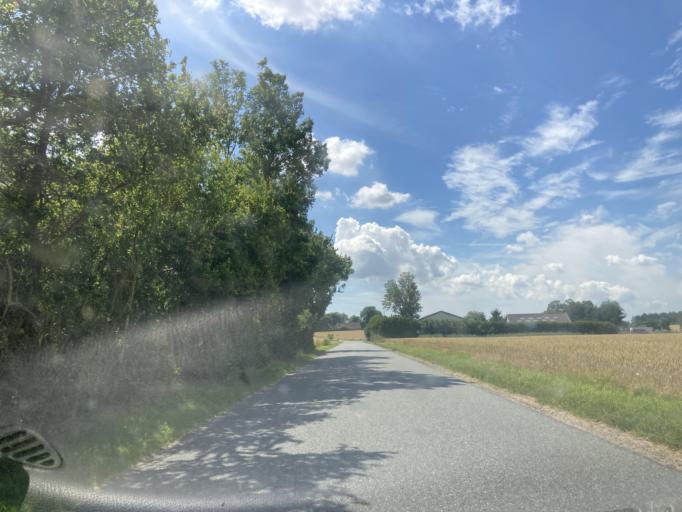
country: DK
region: Zealand
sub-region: Faxe Kommune
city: Haslev
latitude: 55.3550
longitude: 11.9489
